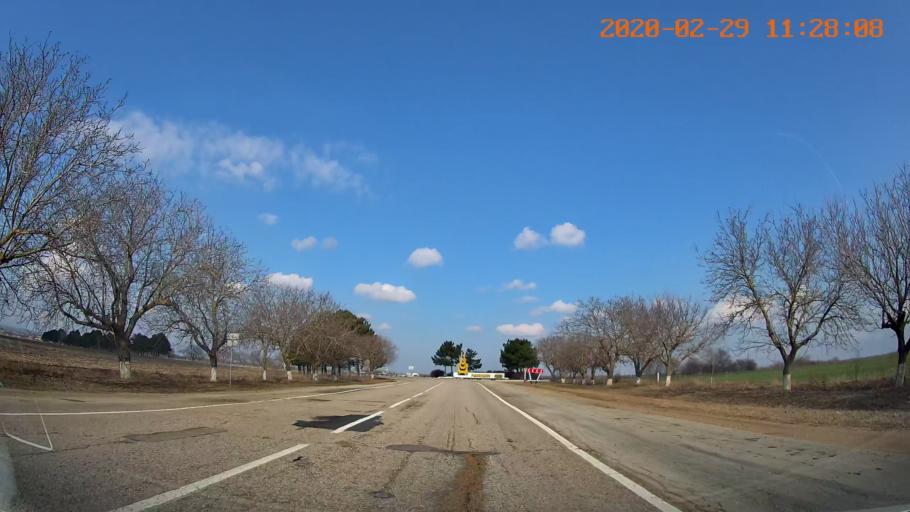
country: MD
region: Telenesti
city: Cocieri
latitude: 47.4789
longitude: 29.1396
